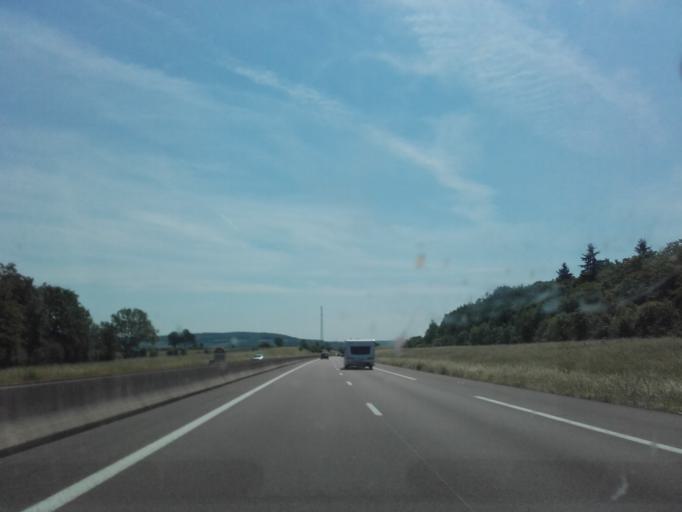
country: FR
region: Bourgogne
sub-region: Departement de la Cote-d'Or
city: Vitteaux
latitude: 47.3505
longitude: 4.4514
